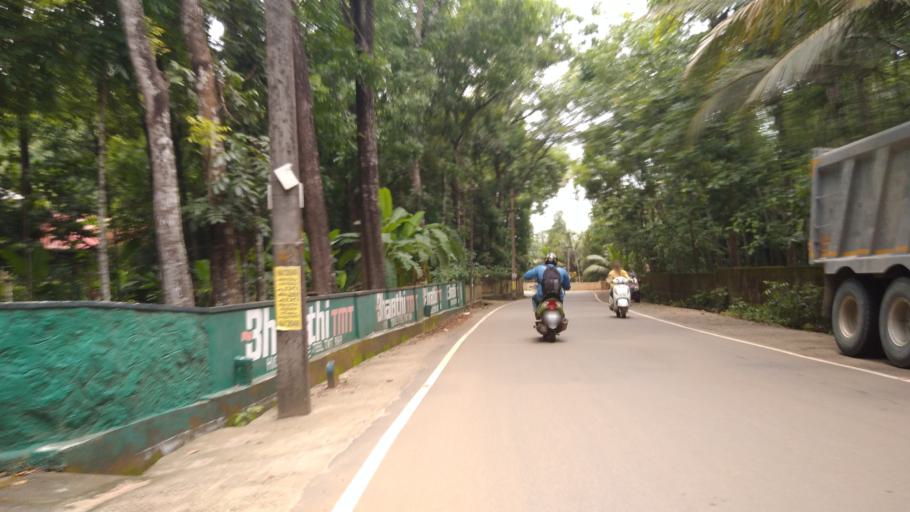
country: IN
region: Kerala
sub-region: Ernakulam
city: Perumpavur
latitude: 10.1222
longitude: 76.5517
